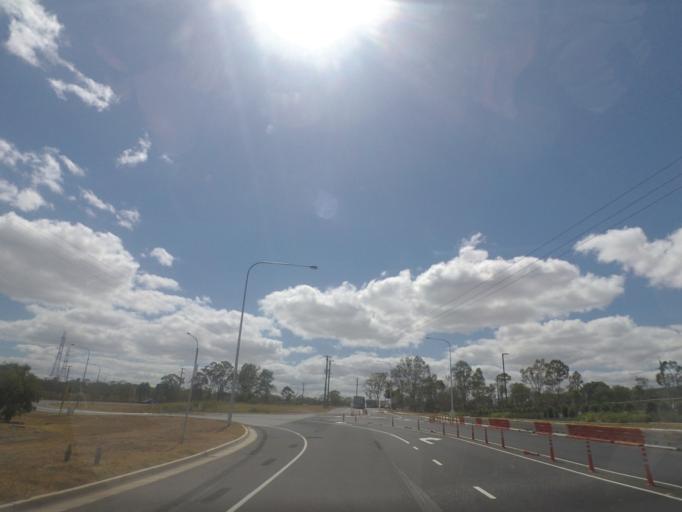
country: AU
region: Queensland
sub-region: Ipswich
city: Bundamba
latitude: -27.5890
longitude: 152.8220
